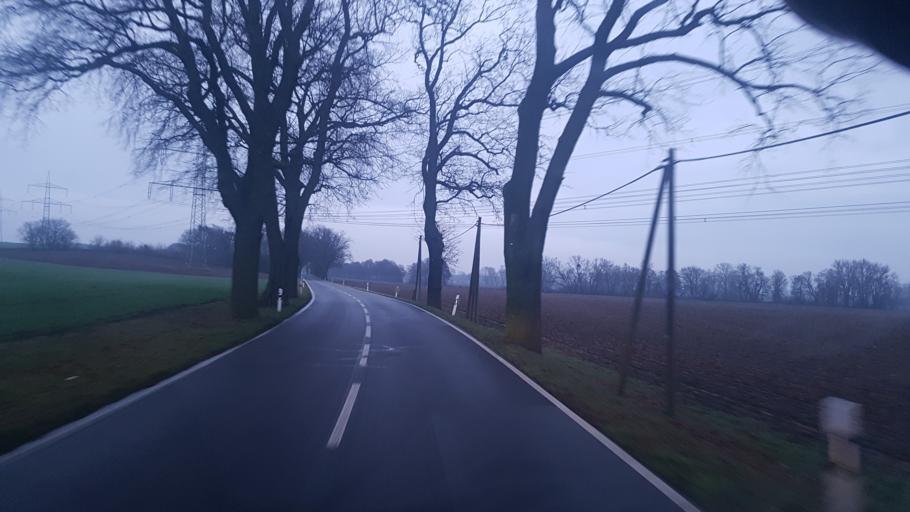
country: DE
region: Brandenburg
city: Trebbin
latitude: 52.2459
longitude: 13.2130
